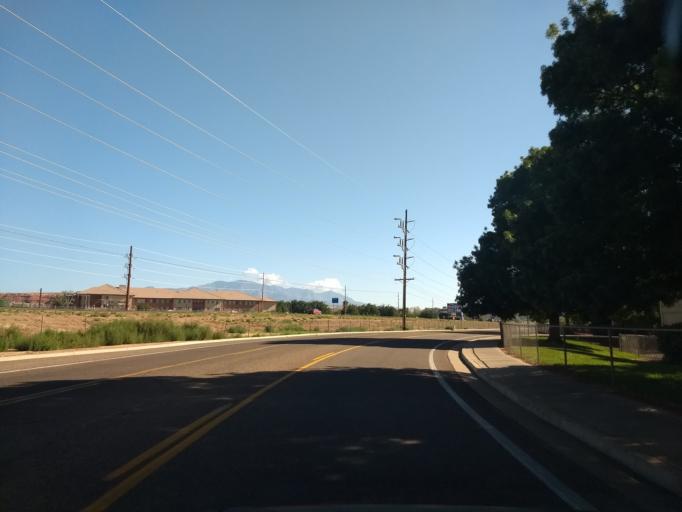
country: US
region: Utah
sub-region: Washington County
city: Saint George
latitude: 37.0898
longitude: -113.5747
